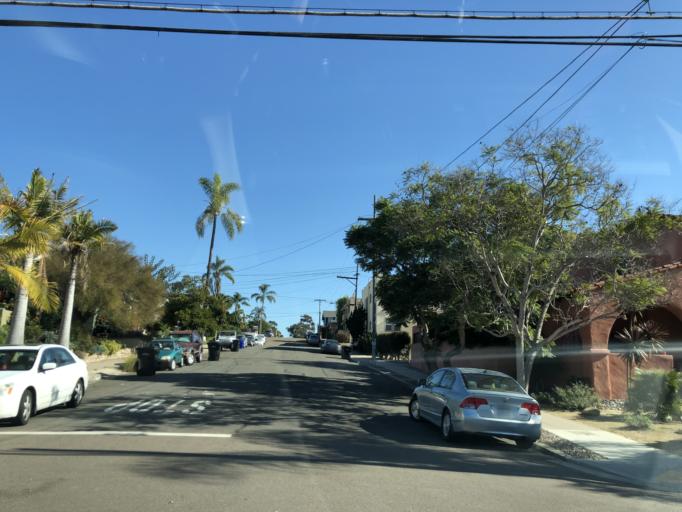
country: US
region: California
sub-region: San Diego County
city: San Diego
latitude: 32.7255
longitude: -117.1321
